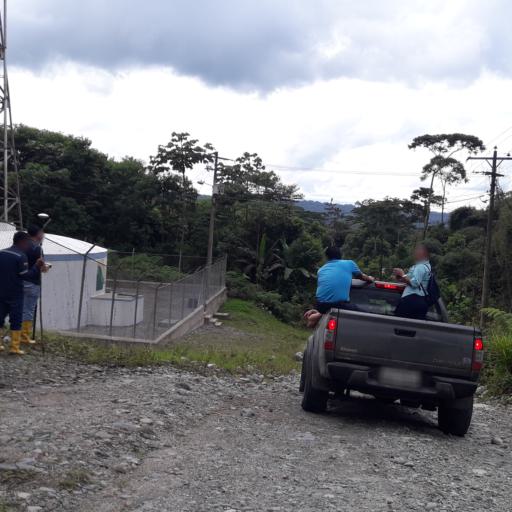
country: EC
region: Napo
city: Archidona
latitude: -0.9430
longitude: -77.8846
